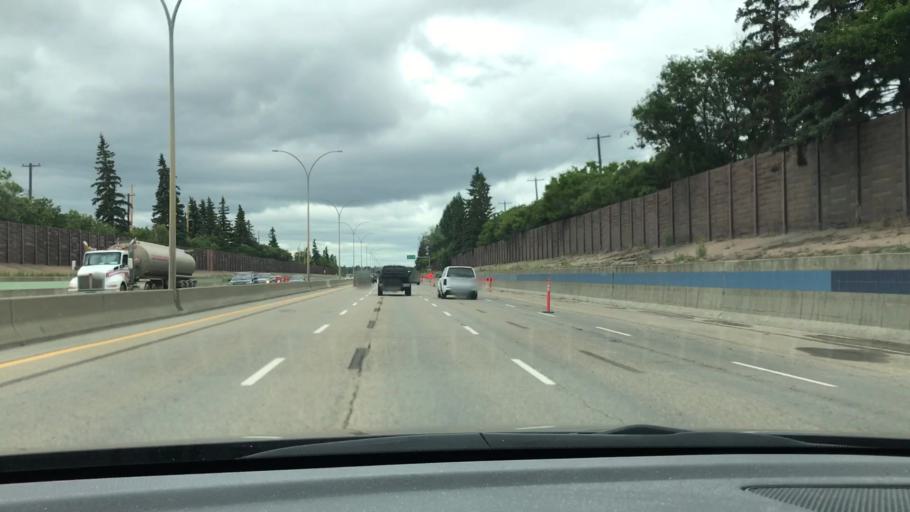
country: CA
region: Alberta
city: Edmonton
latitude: 53.4832
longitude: -113.5290
